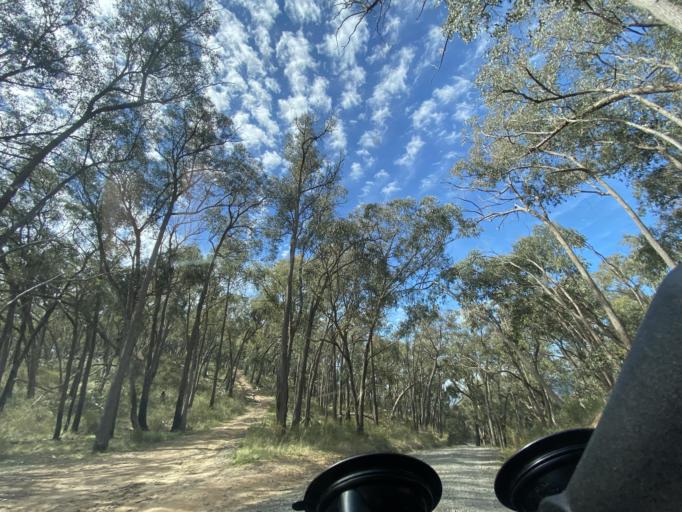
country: AU
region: Victoria
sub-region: Mansfield
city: Mansfield
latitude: -36.8006
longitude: 146.1110
